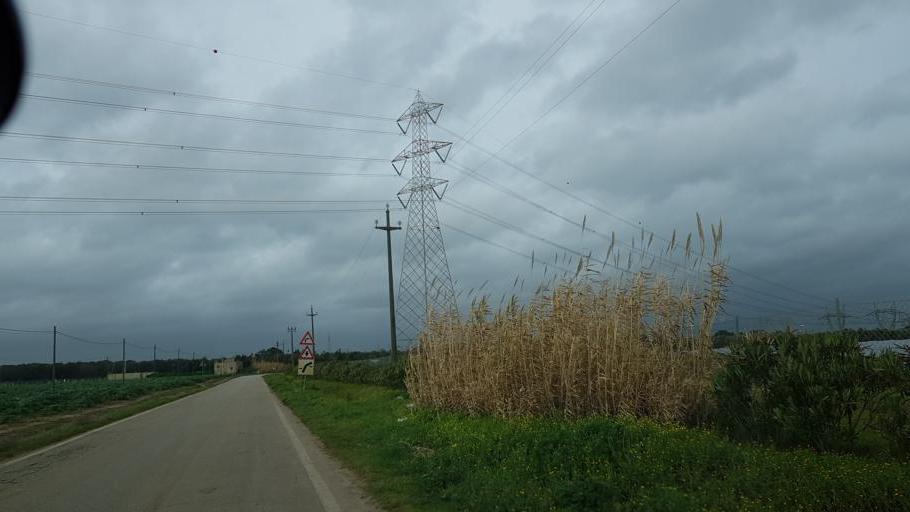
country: IT
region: Apulia
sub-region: Provincia di Brindisi
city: Brindisi
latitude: 40.5946
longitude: 17.9035
